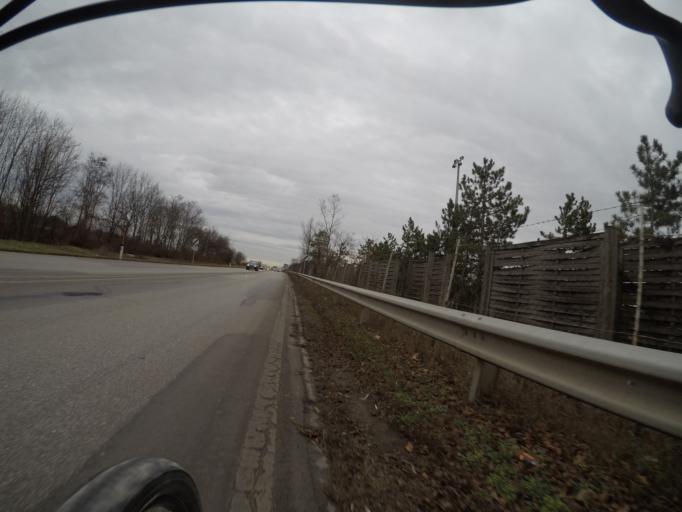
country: AT
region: Lower Austria
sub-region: Politischer Bezirk Modling
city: Wiener Neudorf
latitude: 48.1017
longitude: 16.3109
